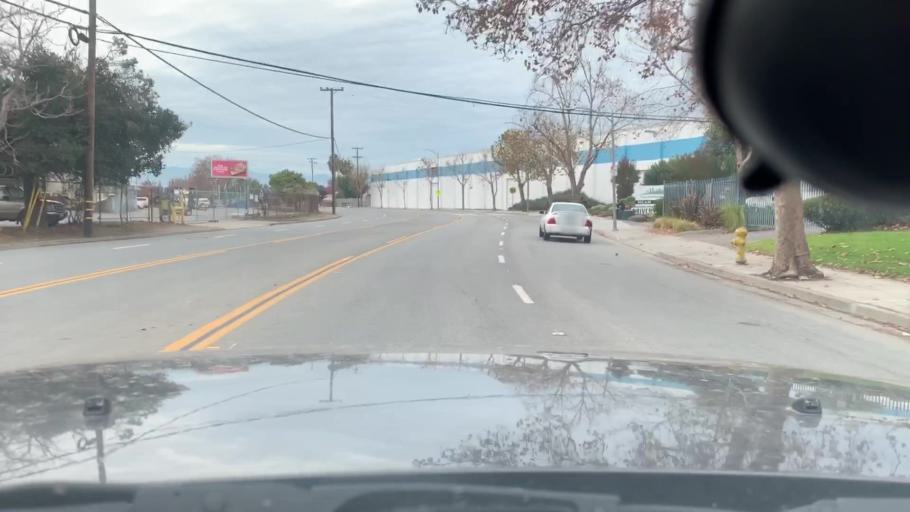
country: US
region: California
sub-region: Santa Clara County
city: San Jose
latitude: 37.3182
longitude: -121.8694
